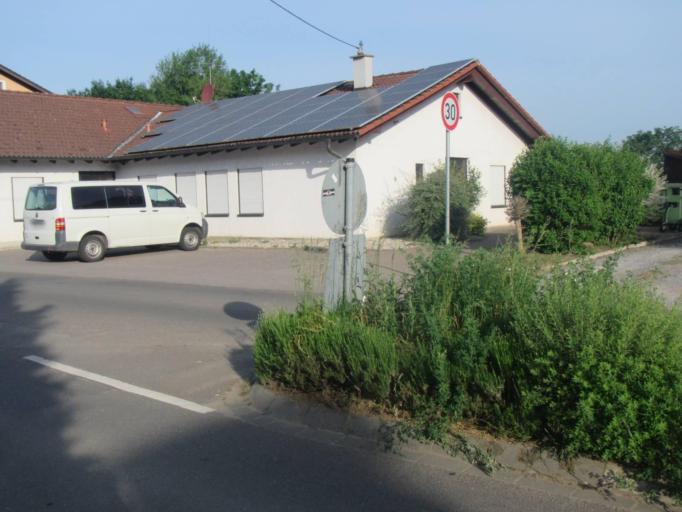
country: DE
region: Rheinland-Pfalz
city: Zeiskam
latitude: 49.2350
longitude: 8.2451
